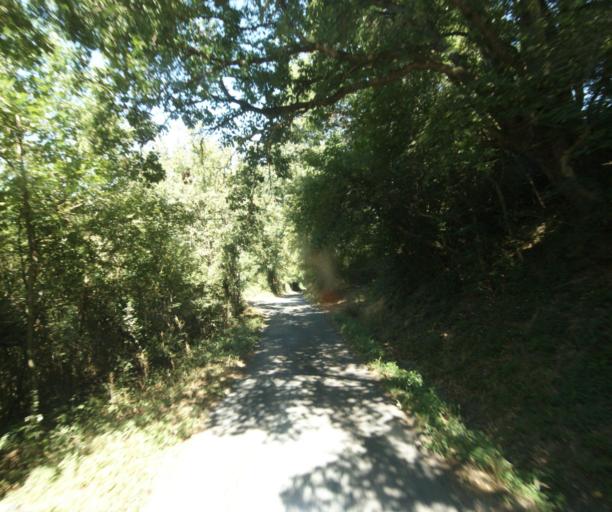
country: FR
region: Rhone-Alpes
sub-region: Departement du Rhone
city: Bessenay
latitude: 45.7938
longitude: 4.5283
